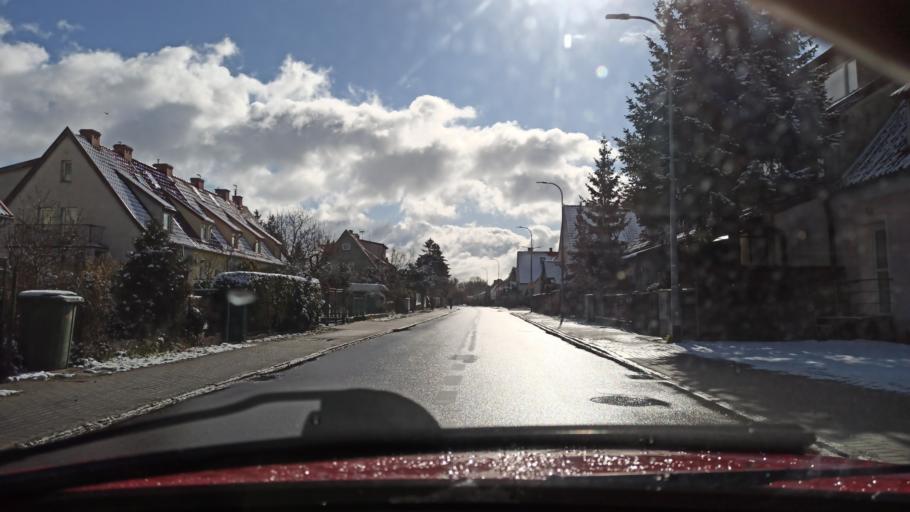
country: PL
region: Warmian-Masurian Voivodeship
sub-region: Powiat elblaski
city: Elblag
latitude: 54.1454
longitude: 19.4061
